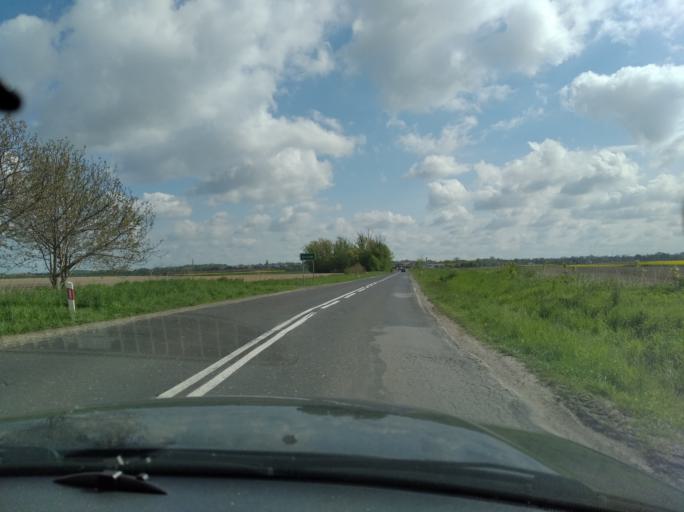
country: PL
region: Subcarpathian Voivodeship
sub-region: Powiat przeworski
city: Przeworsk
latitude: 50.0392
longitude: 22.4734
